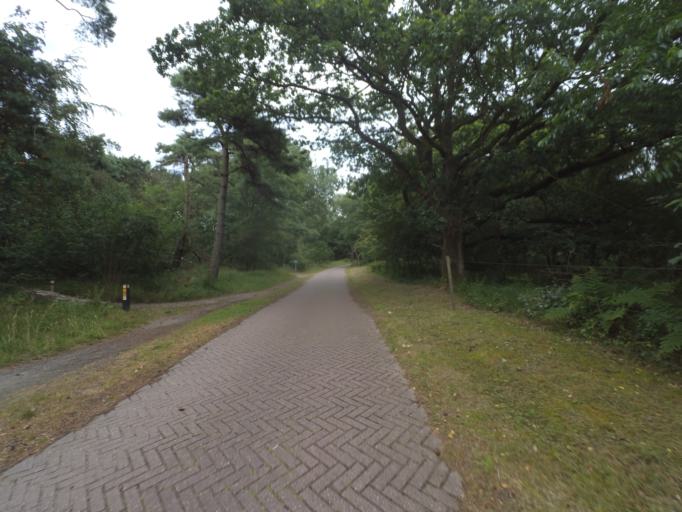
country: NL
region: South Holland
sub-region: Gemeente Leidschendam-Voorburg
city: Voorburg
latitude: 52.1226
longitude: 4.3382
